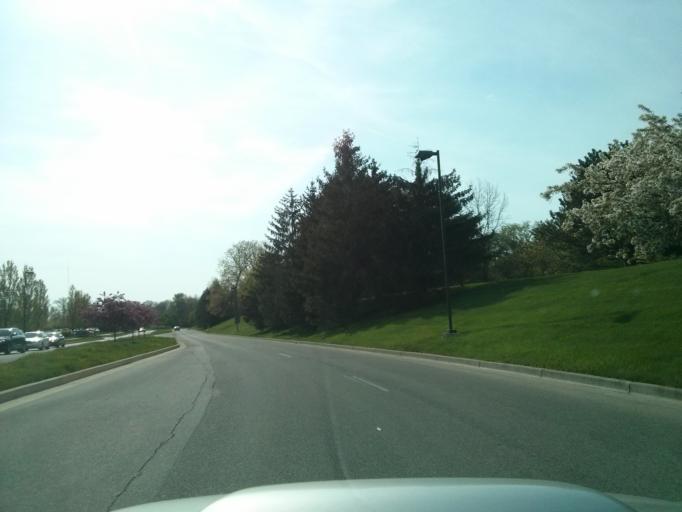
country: US
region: Indiana
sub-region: Marion County
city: Meridian Hills
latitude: 39.9328
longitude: -86.1471
